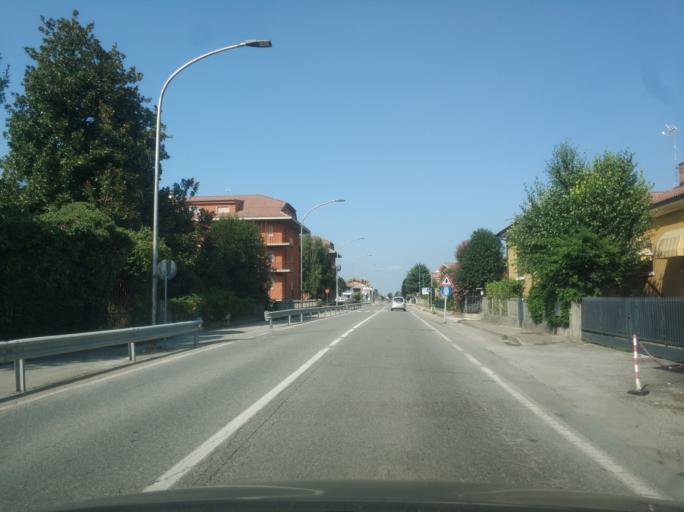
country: IT
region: Piedmont
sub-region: Provincia di Cuneo
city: Centallo
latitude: 44.5034
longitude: 7.5853
